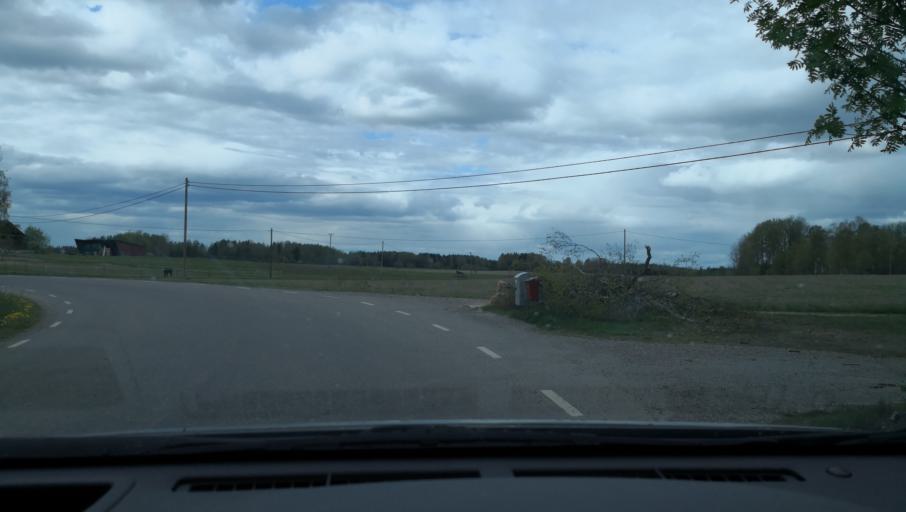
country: SE
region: Dalarna
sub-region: Avesta Kommun
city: Avesta
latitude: 60.0197
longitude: 16.2856
